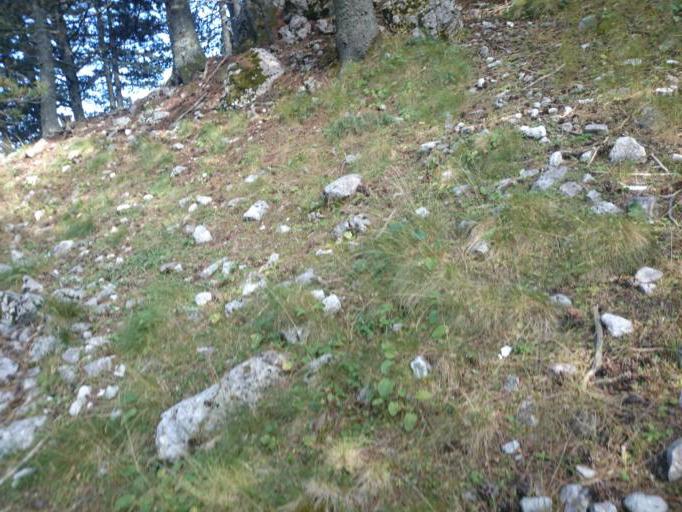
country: AL
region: Elbasan
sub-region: Rrethi i Gramshit
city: Kushove
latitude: 40.7270
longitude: 20.1426
